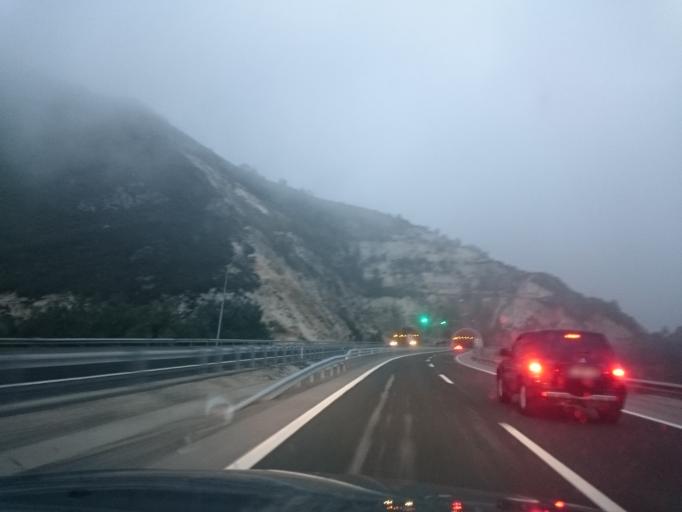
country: ES
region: Castille and Leon
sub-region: Provincia de Leon
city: Sena de Luna
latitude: 42.9877
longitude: -5.8201
